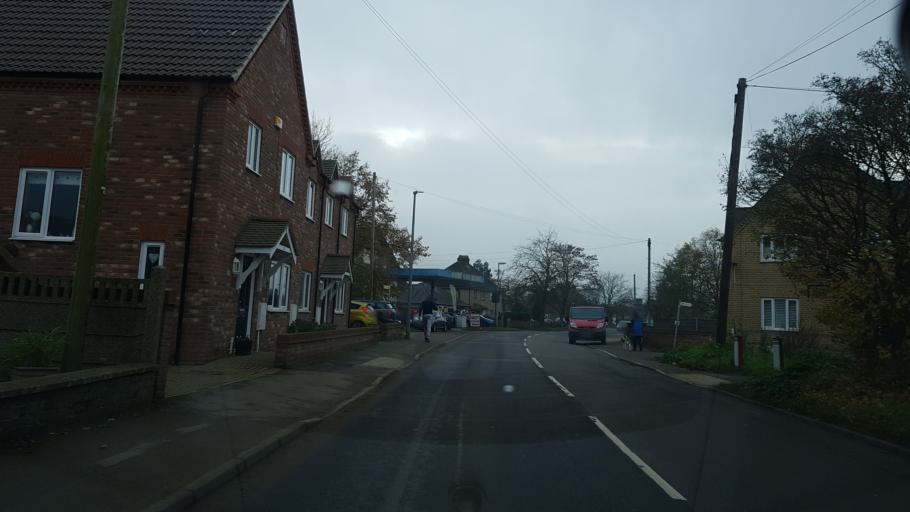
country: GB
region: England
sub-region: Central Bedfordshire
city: Biggleswade
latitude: 52.0958
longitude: -0.2513
